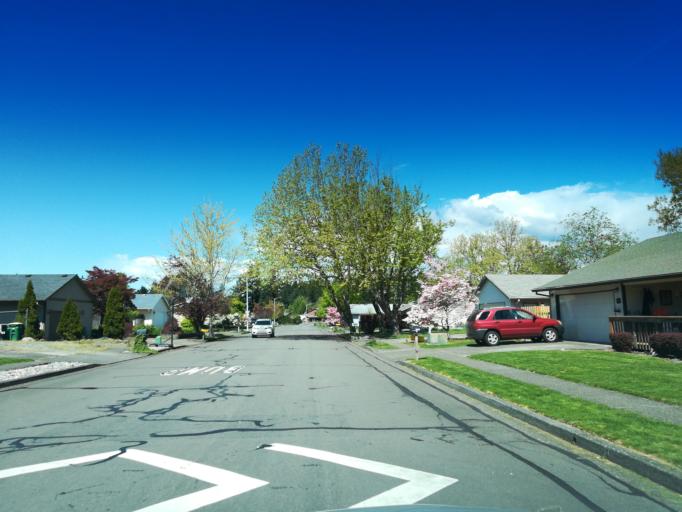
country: US
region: Oregon
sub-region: Multnomah County
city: Troutdale
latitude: 45.5242
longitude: -122.3802
